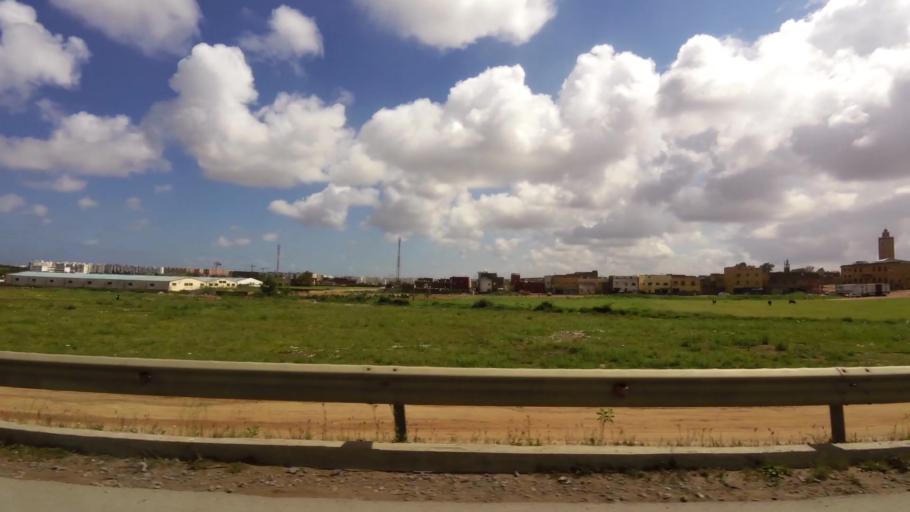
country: MA
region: Grand Casablanca
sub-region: Nouaceur
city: Dar Bouazza
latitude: 33.5392
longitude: -7.7129
